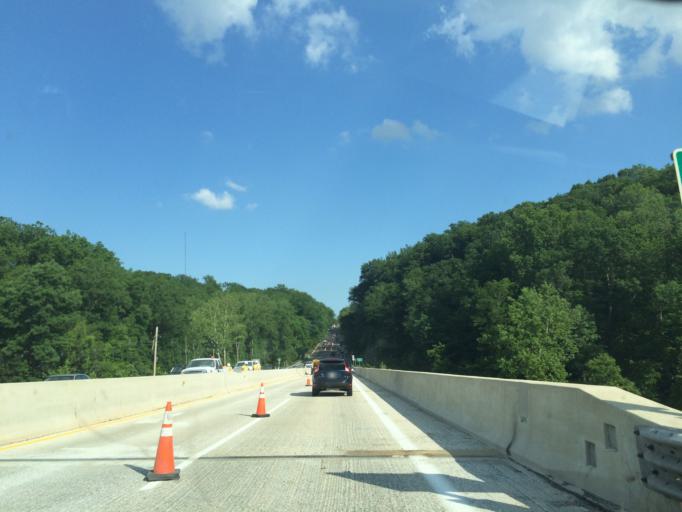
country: US
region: Maryland
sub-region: Howard County
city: Ellicott City
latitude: 39.2954
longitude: -76.7793
